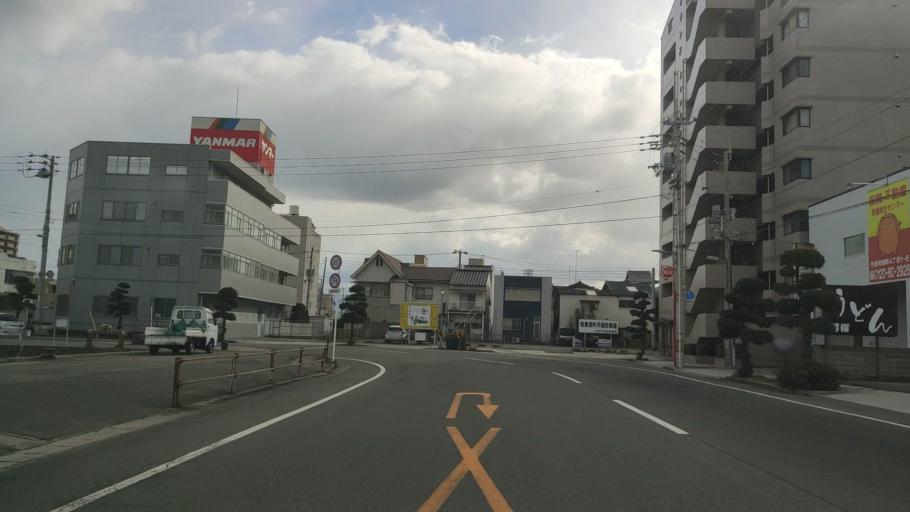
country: JP
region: Ehime
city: Saijo
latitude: 34.0661
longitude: 133.0065
